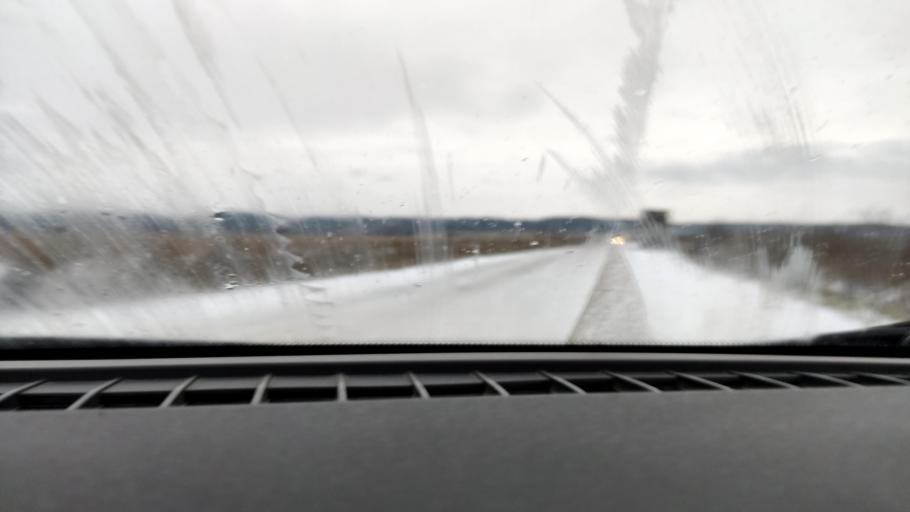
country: RU
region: Perm
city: Kondratovo
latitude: 57.9241
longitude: 56.1671
